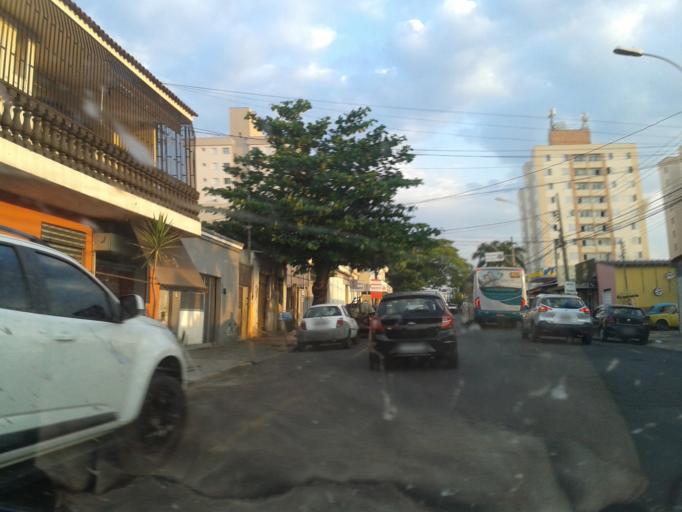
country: BR
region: Minas Gerais
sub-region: Uberlandia
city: Uberlandia
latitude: -18.9061
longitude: -48.2788
